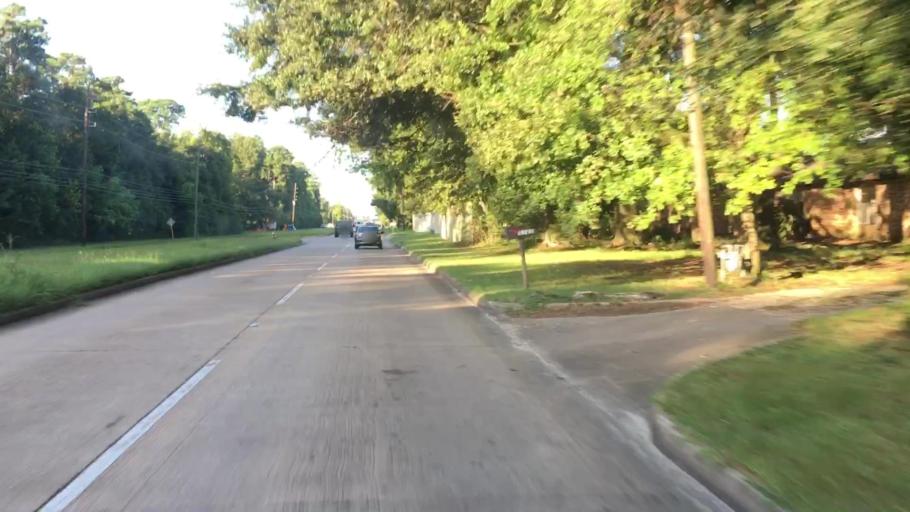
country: US
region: Texas
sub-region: Harris County
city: Humble
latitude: 29.9484
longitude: -95.2750
